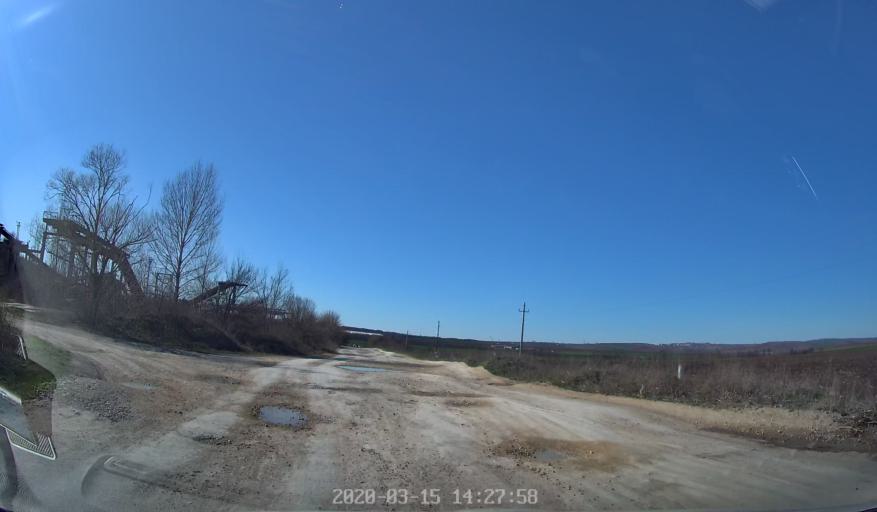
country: MD
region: Orhei
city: Orhei
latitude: 47.3457
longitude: 28.8907
